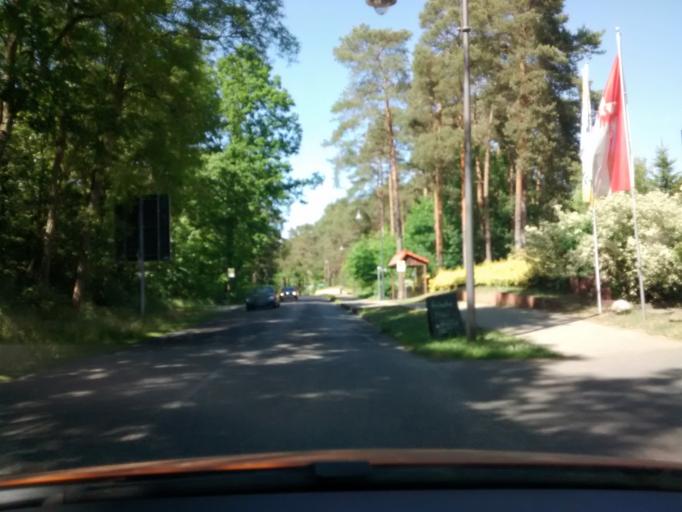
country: DE
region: Brandenburg
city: Diensdorf-Radlow
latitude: 52.2750
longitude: 14.0402
